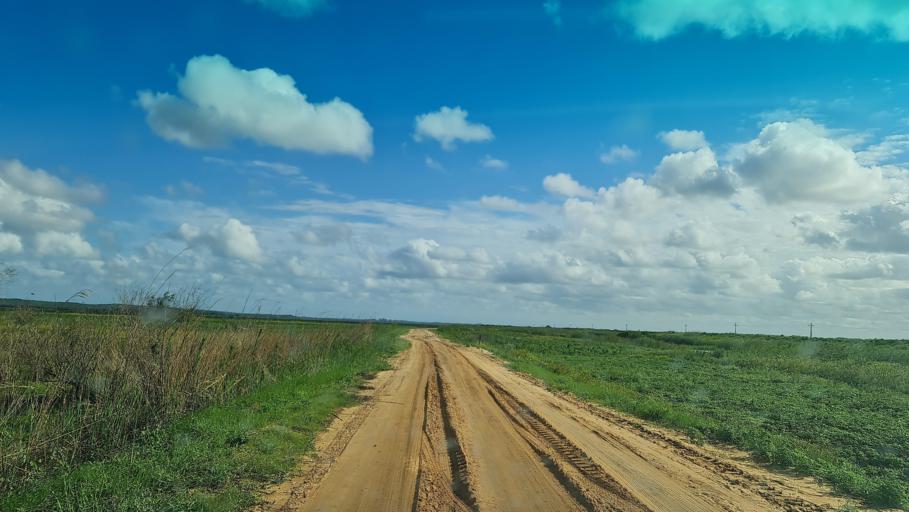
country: MZ
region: Maputo
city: Manhica
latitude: -25.4365
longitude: 32.8619
